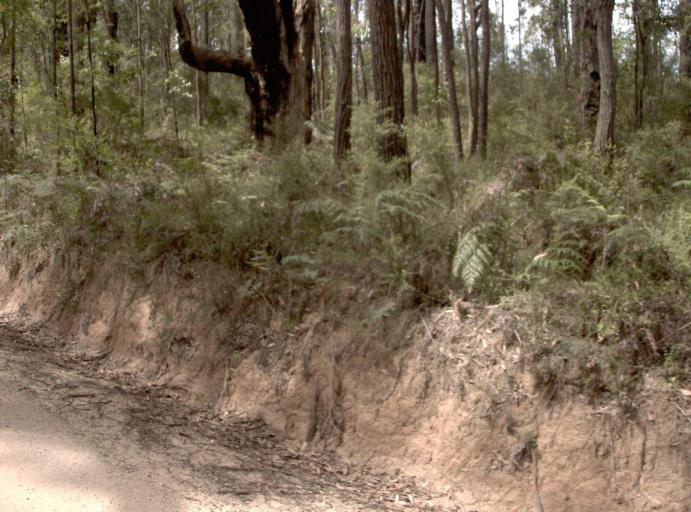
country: AU
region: Victoria
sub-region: East Gippsland
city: Lakes Entrance
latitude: -37.6300
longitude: 148.6760
